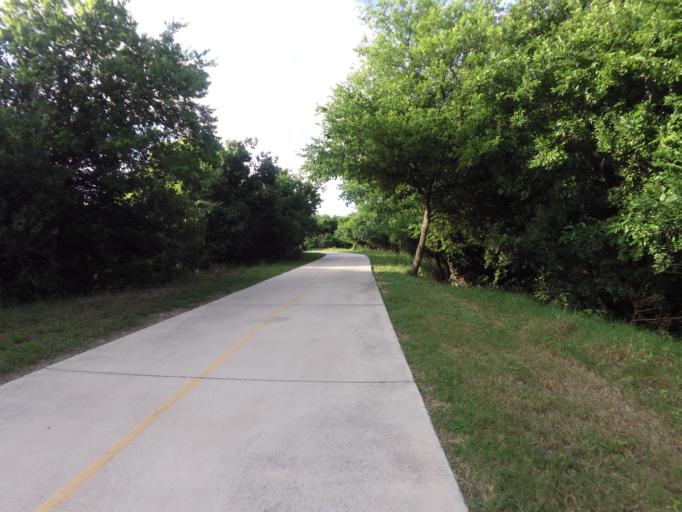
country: US
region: Texas
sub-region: Bexar County
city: Leon Valley
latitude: 29.4751
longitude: -98.6354
